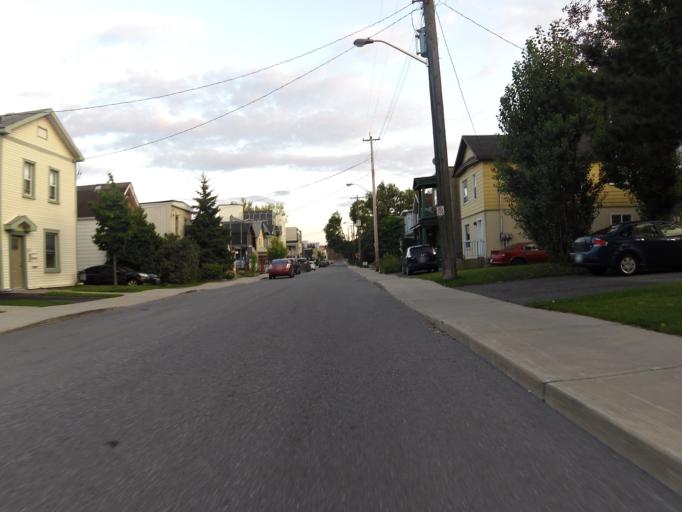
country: CA
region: Ontario
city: Ottawa
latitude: 45.4058
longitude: -75.7271
